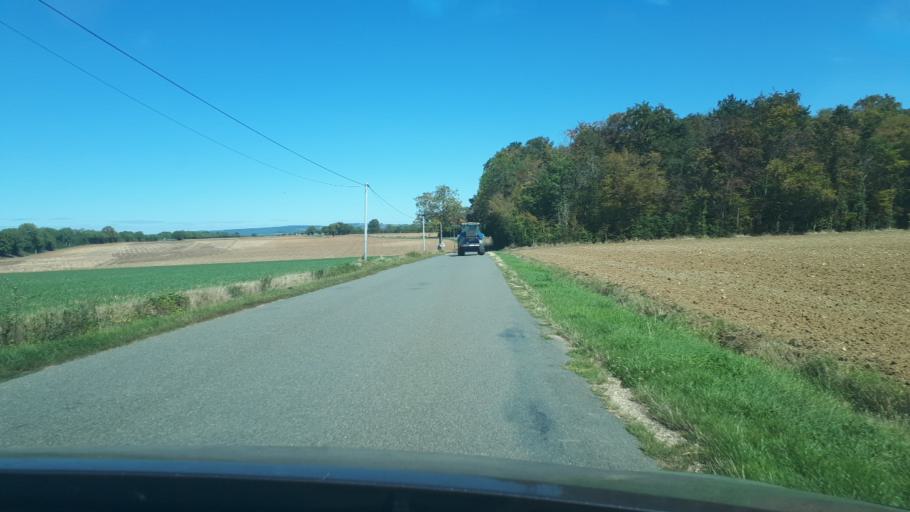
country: FR
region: Centre
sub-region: Departement du Cher
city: Sainte-Solange
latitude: 47.1486
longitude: 2.5605
